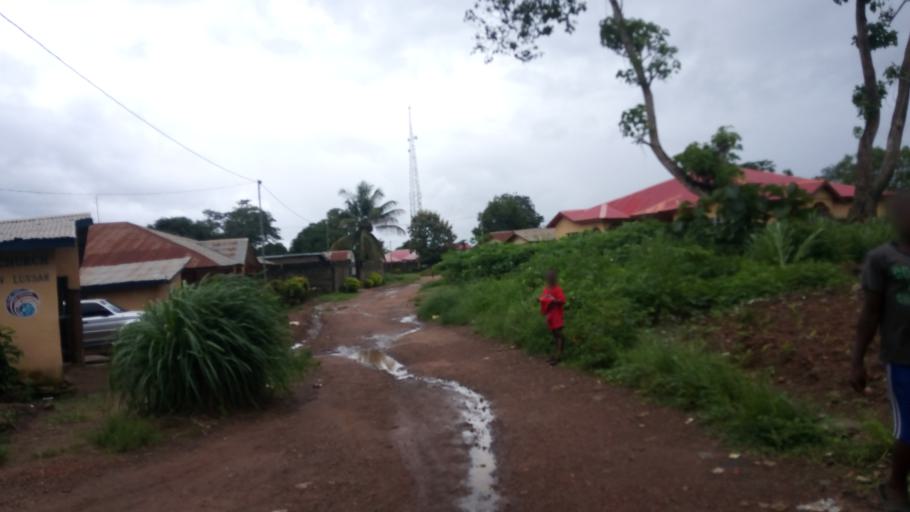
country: SL
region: Northern Province
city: Lunsar
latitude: 8.6917
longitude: -12.5307
